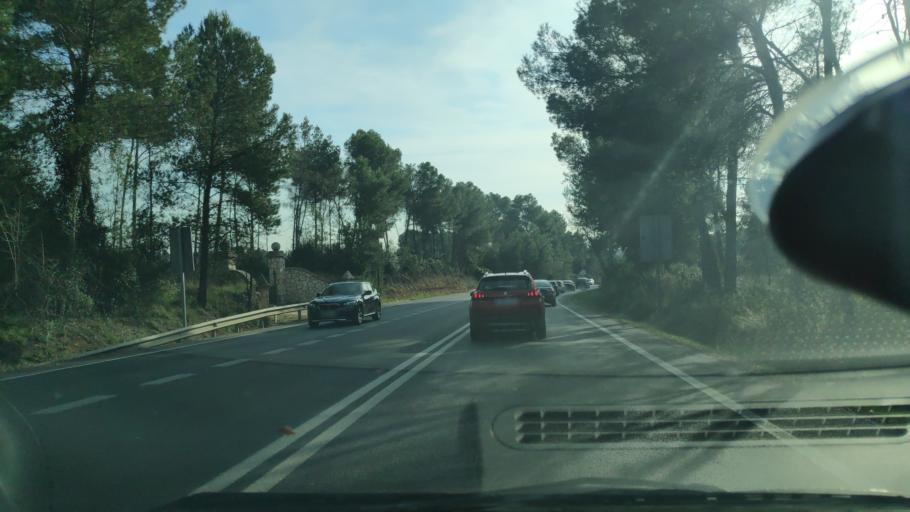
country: ES
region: Catalonia
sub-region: Provincia de Barcelona
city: Castellar del Valles
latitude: 41.5857
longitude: 2.0903
